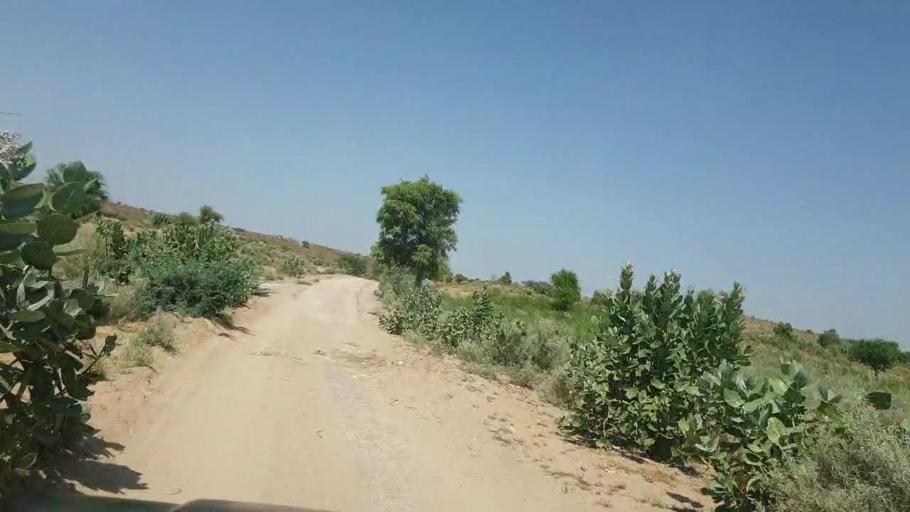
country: PK
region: Sindh
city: Chor
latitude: 25.3822
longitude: 70.3135
